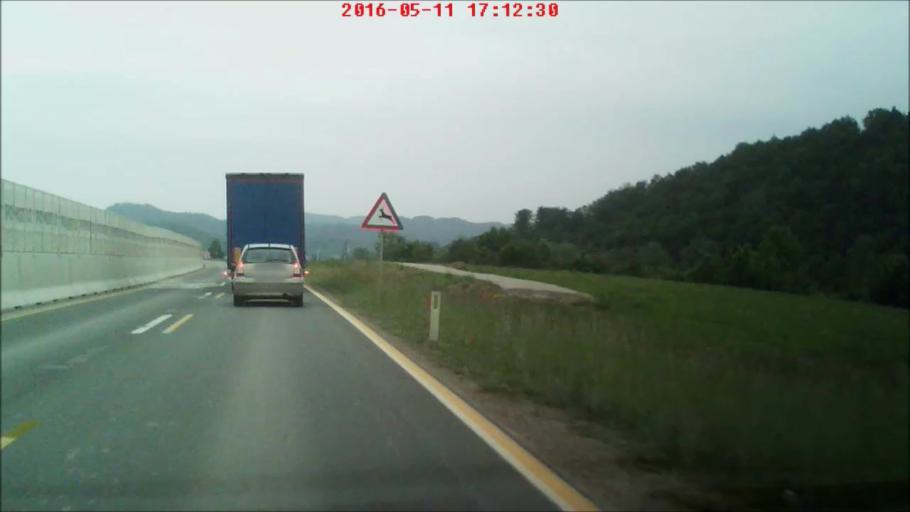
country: SI
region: Podlehnik
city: Podlehnik
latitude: 46.3467
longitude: 15.8691
